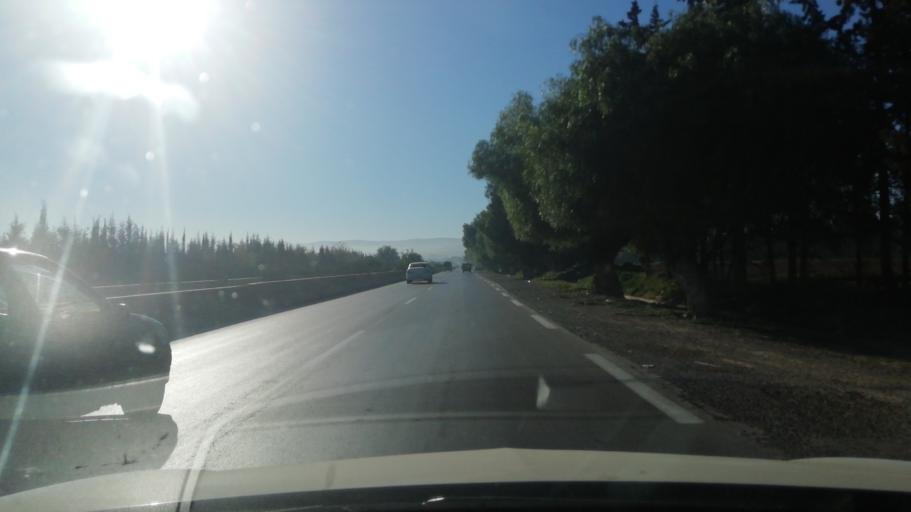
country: DZ
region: Tlemcen
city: Hennaya
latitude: 34.9761
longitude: -1.3804
